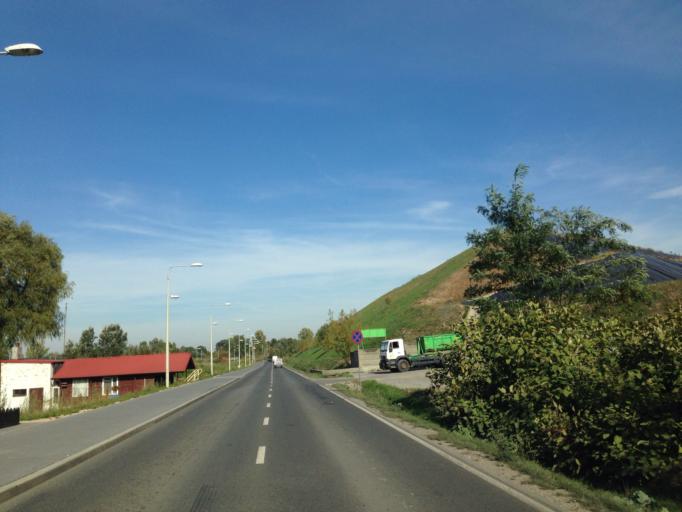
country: PL
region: Masovian Voivodeship
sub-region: Powiat pruszkowski
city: Pruszkow
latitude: 52.1761
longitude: 20.7719
